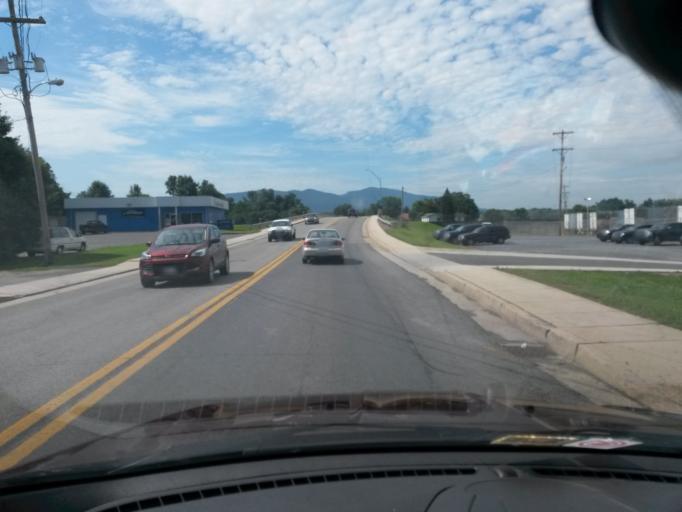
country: US
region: West Virginia
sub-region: Hardy County
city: Moorefield
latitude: 39.0575
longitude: -78.9700
